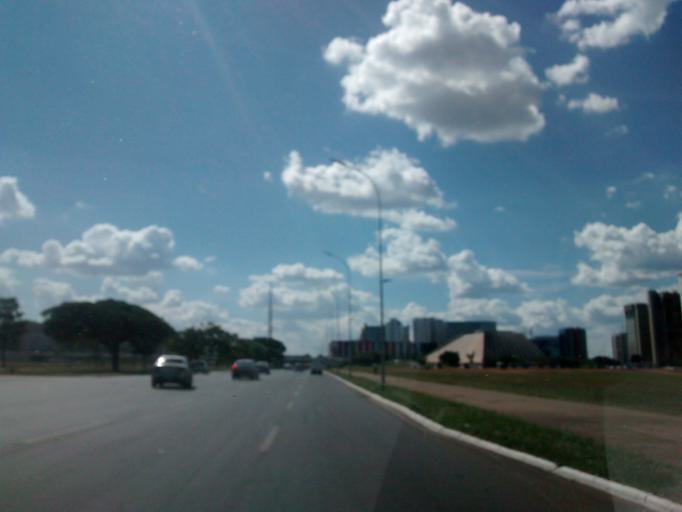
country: BR
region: Federal District
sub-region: Brasilia
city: Brasilia
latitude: -15.7948
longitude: -47.8763
